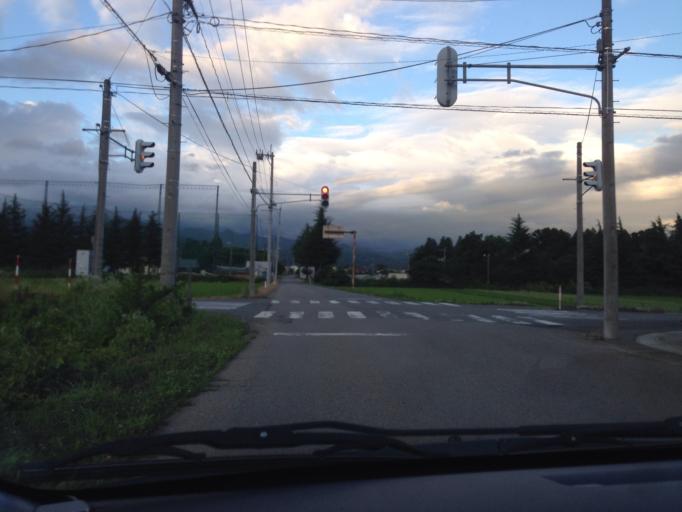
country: JP
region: Fukushima
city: Kitakata
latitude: 37.6732
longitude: 139.8650
